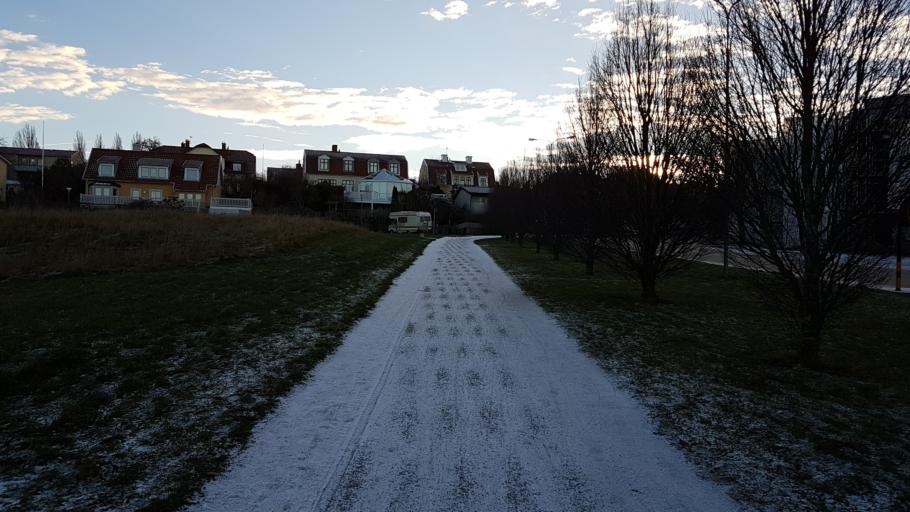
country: SE
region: Gotland
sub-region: Gotland
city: Visby
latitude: 57.6473
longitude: 18.3013
